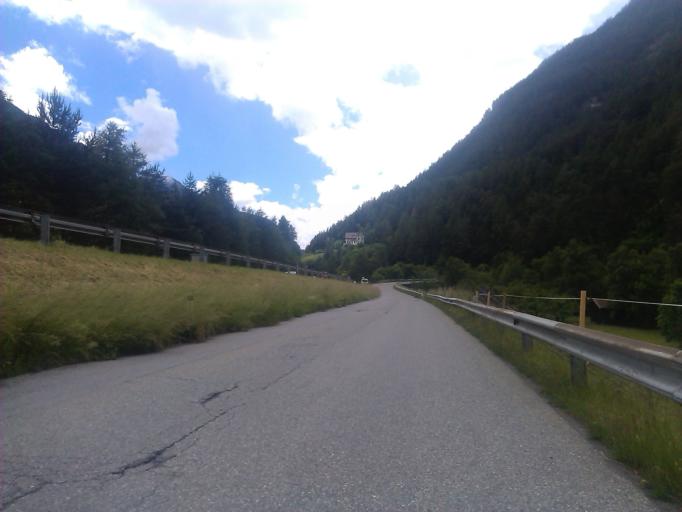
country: AT
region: Tyrol
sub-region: Politischer Bezirk Landeck
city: Serfaus
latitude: 47.0146
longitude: 10.6026
